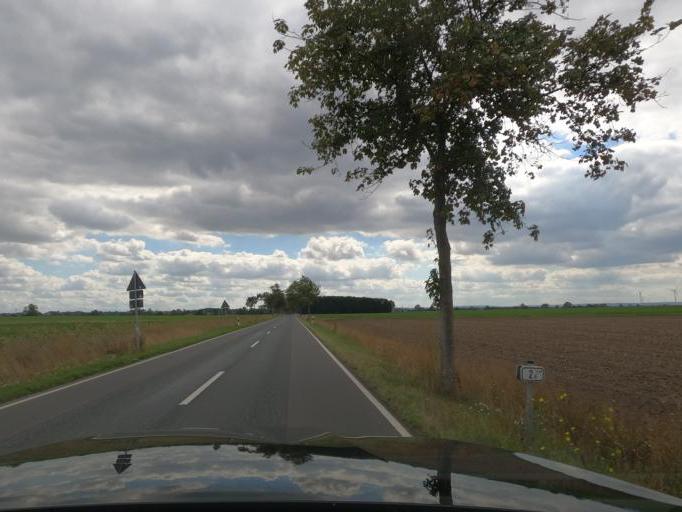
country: DE
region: Lower Saxony
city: Hohenhameln
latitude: 52.2843
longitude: 10.0436
